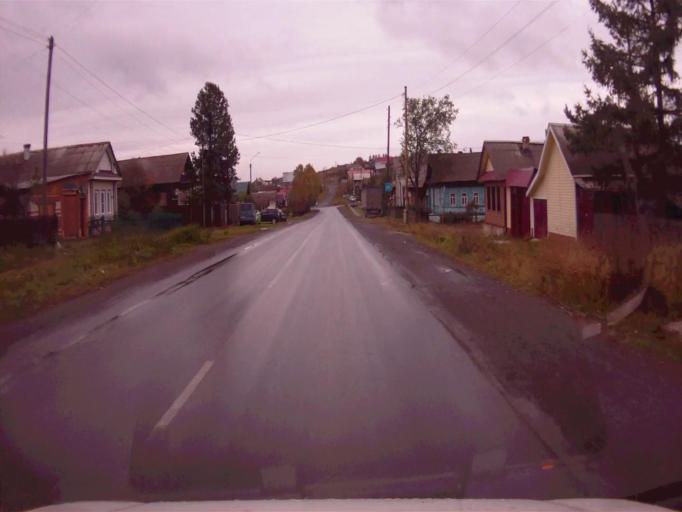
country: RU
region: Chelyabinsk
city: Verkhniy Ufaley
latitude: 56.0565
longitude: 60.2043
